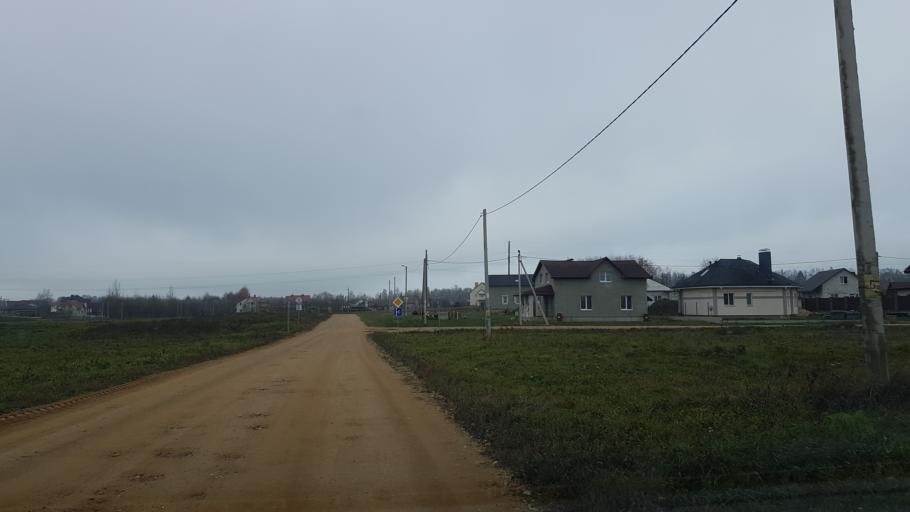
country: BY
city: Fanipol
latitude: 53.7296
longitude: 27.3199
